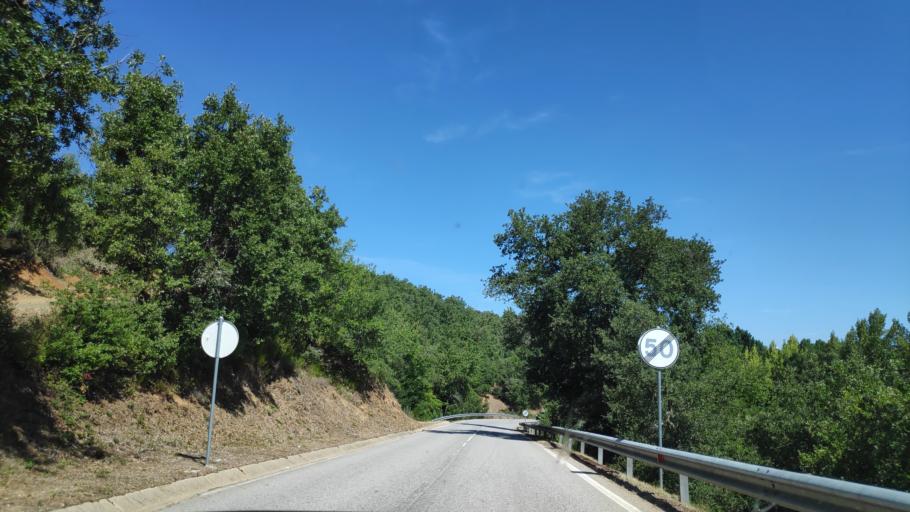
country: PT
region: Braganca
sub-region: Braganca Municipality
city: Braganca
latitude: 41.8476
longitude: -6.7471
